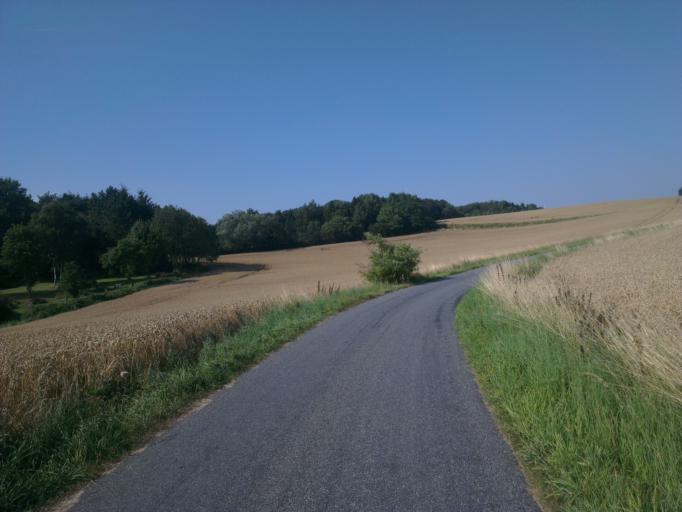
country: DK
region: Capital Region
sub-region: Frederikssund Kommune
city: Skibby
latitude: 55.7598
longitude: 11.9416
